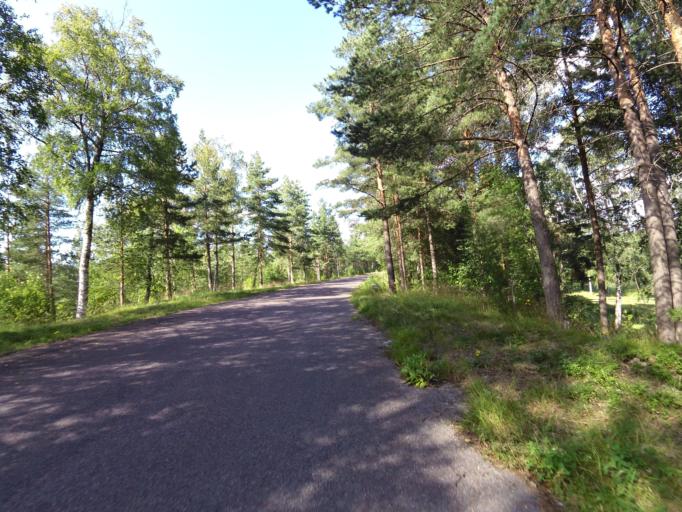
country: SE
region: Dalarna
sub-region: Faluns Kommun
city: Svardsjo
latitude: 60.6567
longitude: 15.8407
